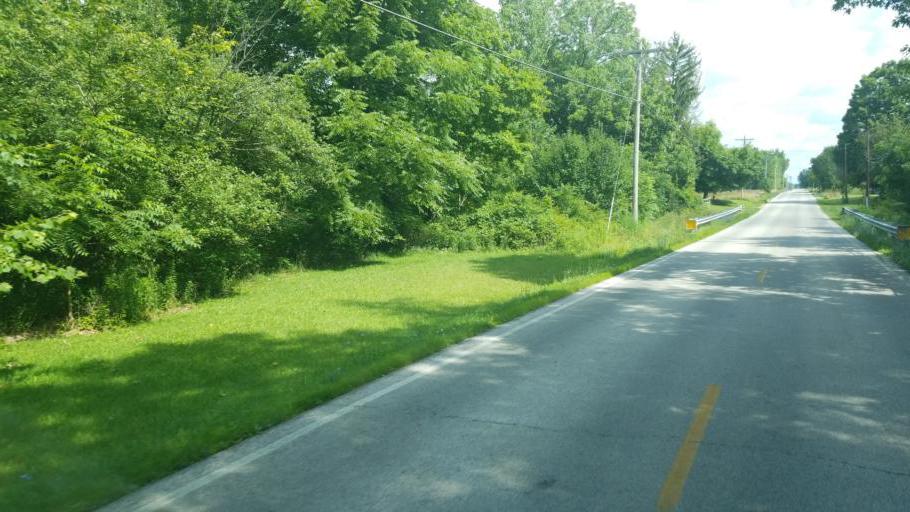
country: US
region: Ohio
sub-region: Delaware County
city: Ashley
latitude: 40.3118
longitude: -82.9333
